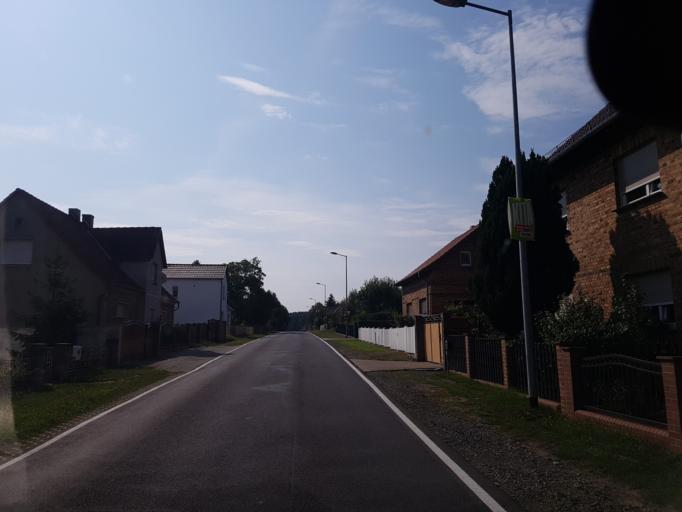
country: DE
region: Brandenburg
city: Lauchhammer
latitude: 51.5168
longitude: 13.7063
